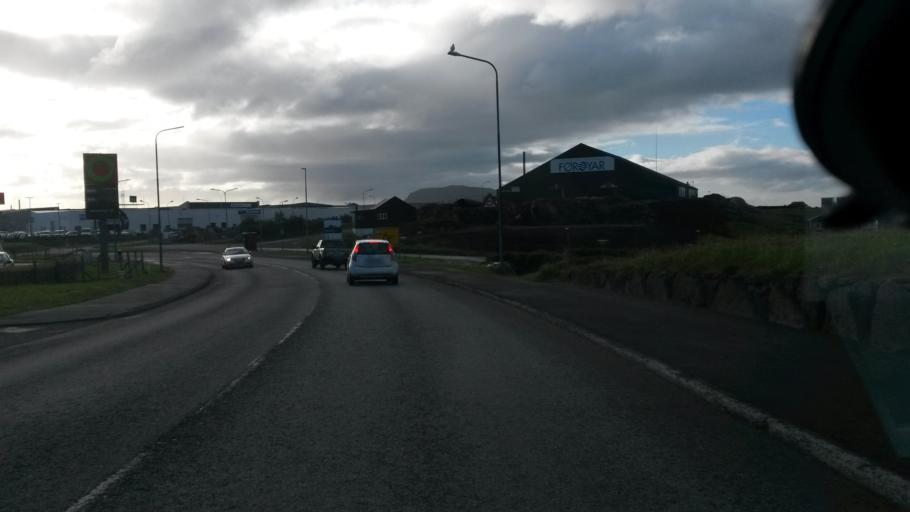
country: FO
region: Streymoy
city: Hoyvik
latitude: 62.0210
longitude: -6.7793
